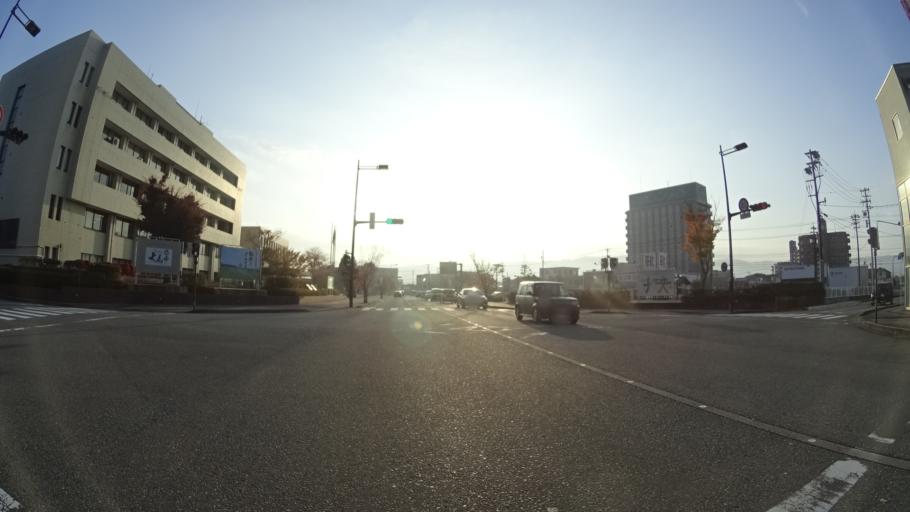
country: JP
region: Ishikawa
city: Nanao
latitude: 37.0430
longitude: 136.9664
